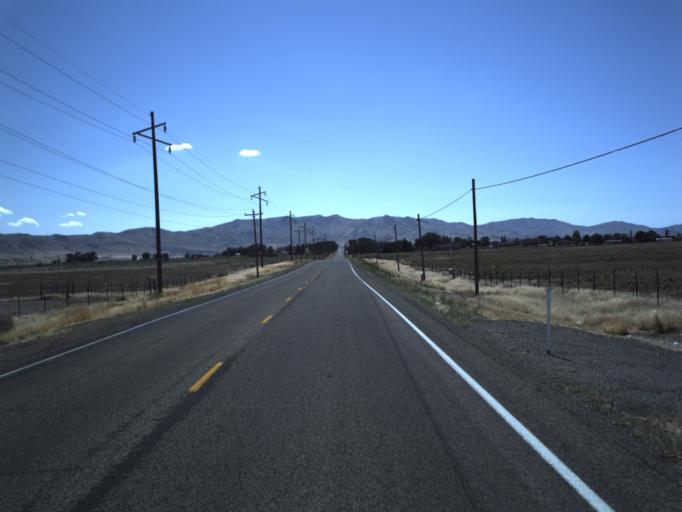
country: US
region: Utah
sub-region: Utah County
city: Genola
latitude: 39.9690
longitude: -111.9568
